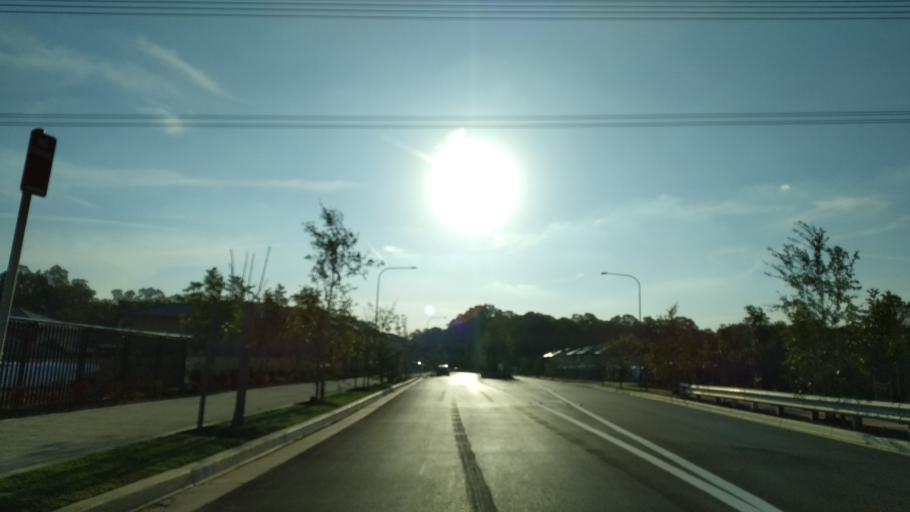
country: AU
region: New South Wales
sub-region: Penrith Municipality
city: Werrington County
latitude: -33.7344
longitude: 150.7513
